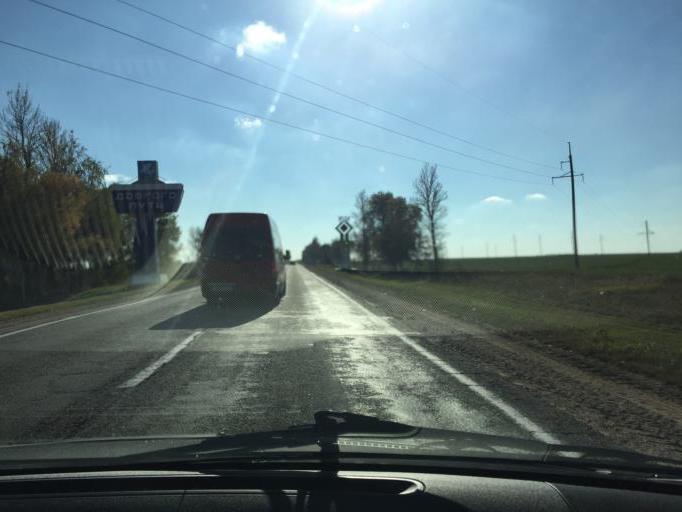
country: BY
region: Minsk
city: Salihorsk
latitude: 52.9048
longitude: 27.4773
